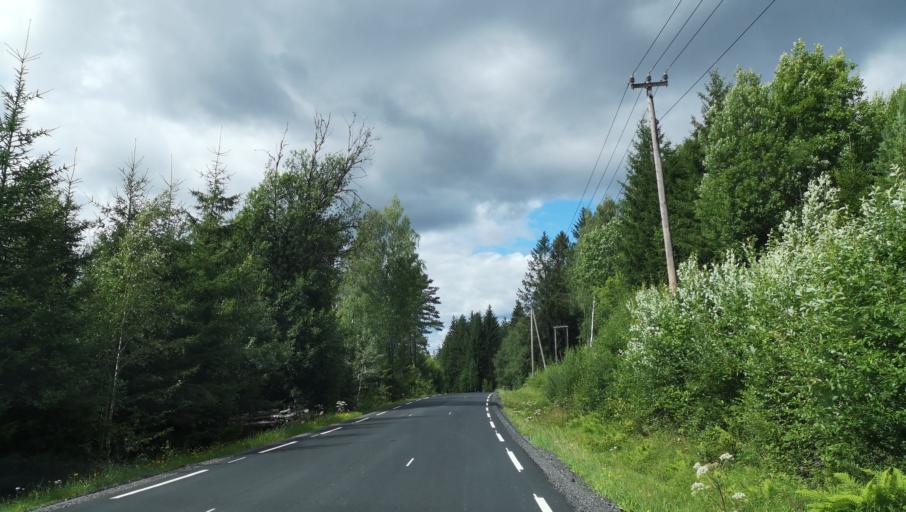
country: NO
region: Ostfold
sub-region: Hobol
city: Tomter
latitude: 59.6802
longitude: 10.9469
